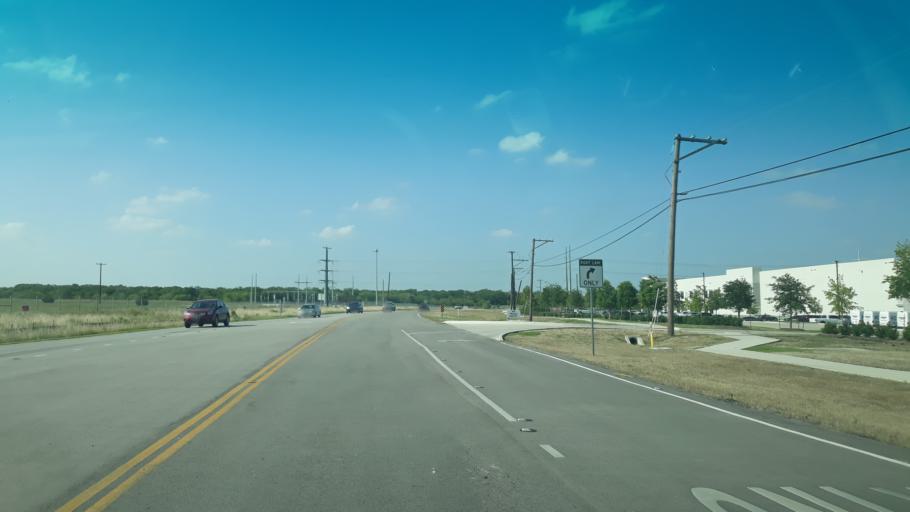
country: US
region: Texas
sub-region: Tarrant County
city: Euless
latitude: 32.8589
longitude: -97.0209
